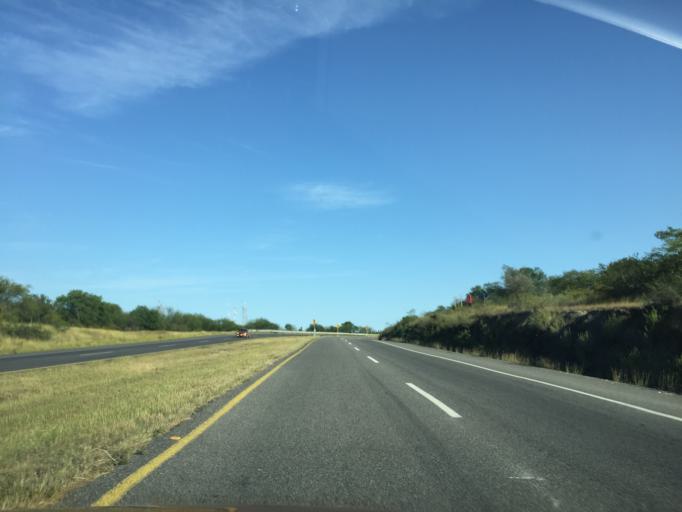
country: MX
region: Nuevo Leon
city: Montemorelos
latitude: 25.1321
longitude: -99.8180
